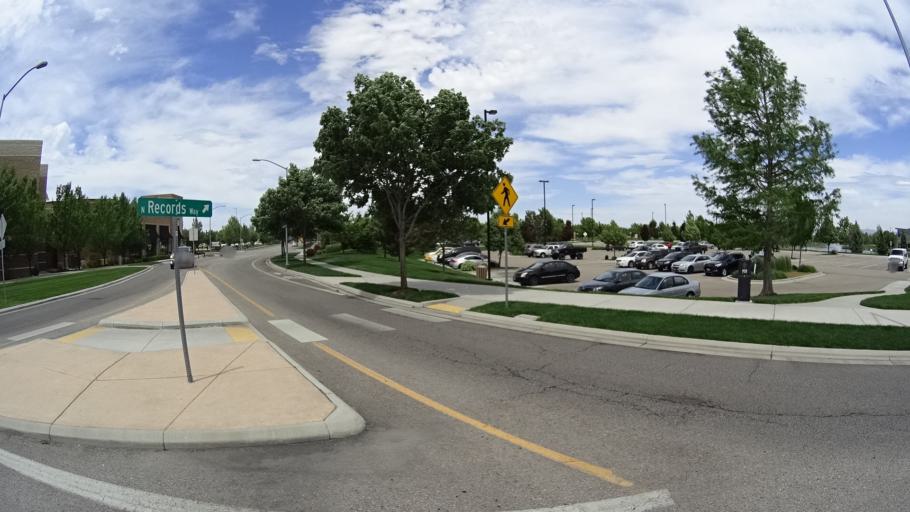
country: US
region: Idaho
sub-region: Ada County
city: Meridian
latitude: 43.6218
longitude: -116.3471
